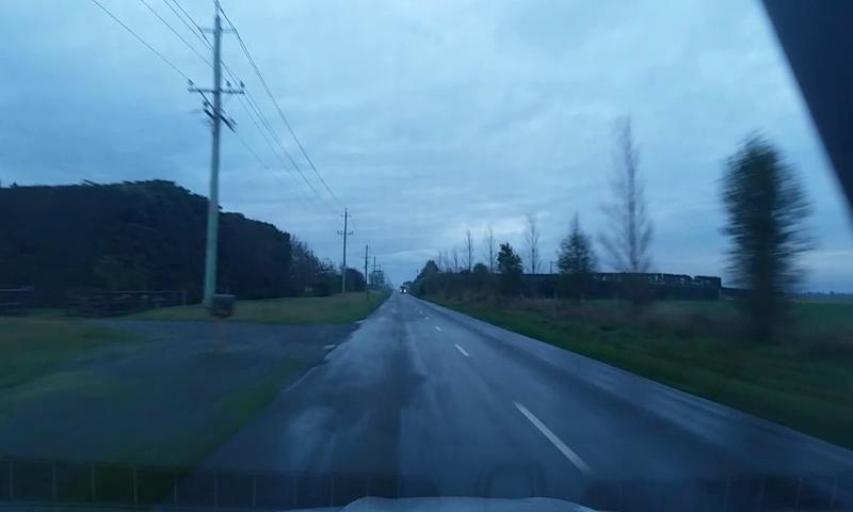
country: NZ
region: Canterbury
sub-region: Ashburton District
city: Rakaia
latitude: -43.7579
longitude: 171.9489
